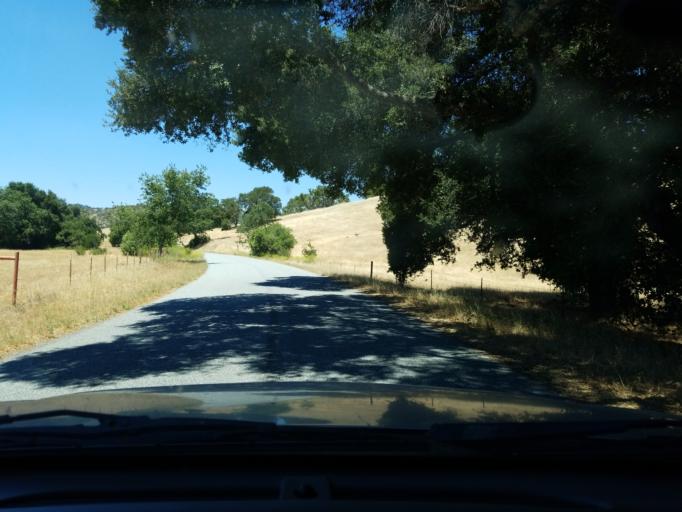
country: US
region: California
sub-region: Monterey County
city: Gonzales
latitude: 36.3941
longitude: -121.5691
